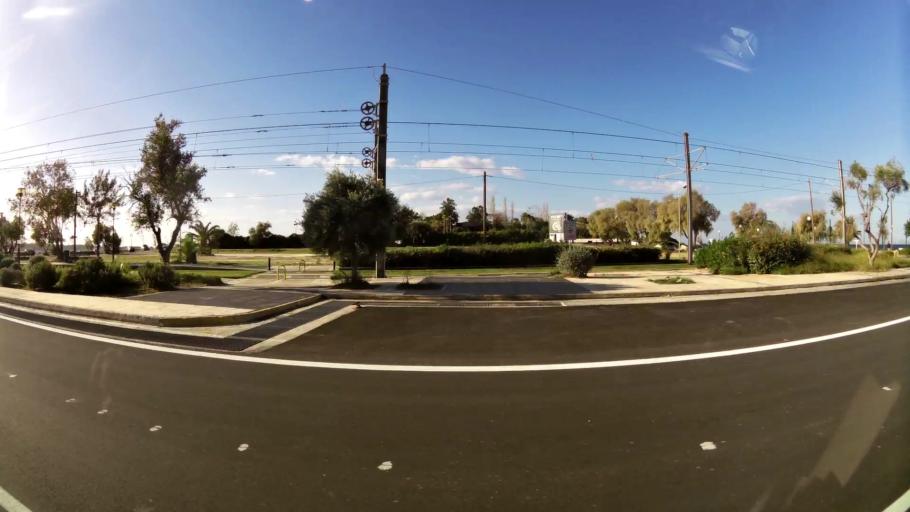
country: GR
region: Attica
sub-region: Nomarchia Athinas
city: Elliniko
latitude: 37.8681
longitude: 23.7379
